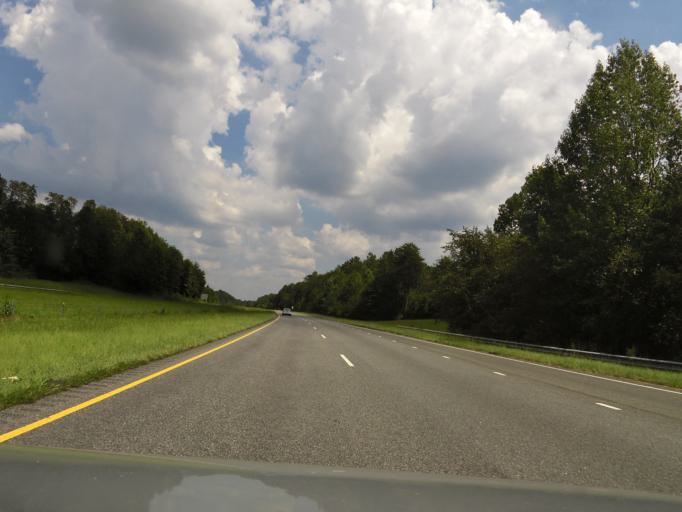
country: US
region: North Carolina
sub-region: Polk County
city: Columbus
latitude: 35.2837
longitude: -82.1085
